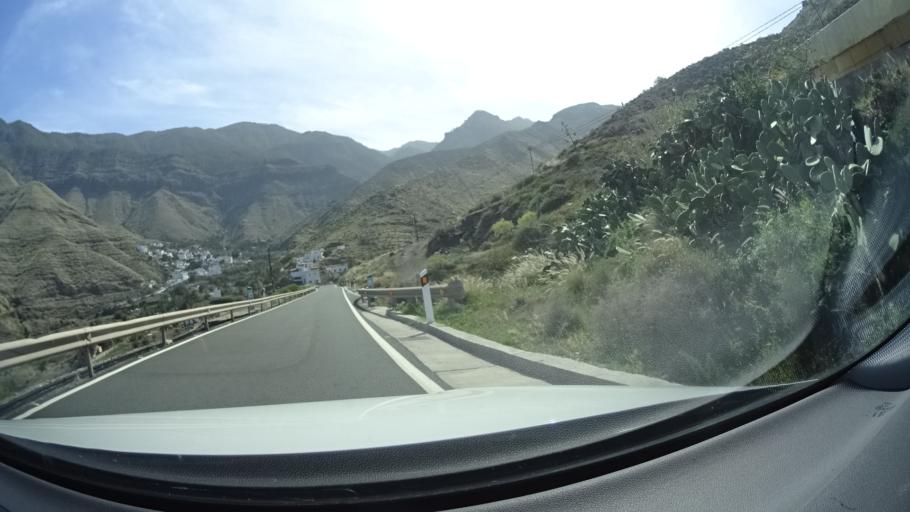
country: ES
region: Canary Islands
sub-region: Provincia de Las Palmas
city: Agaete
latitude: 28.0464
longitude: -15.7329
